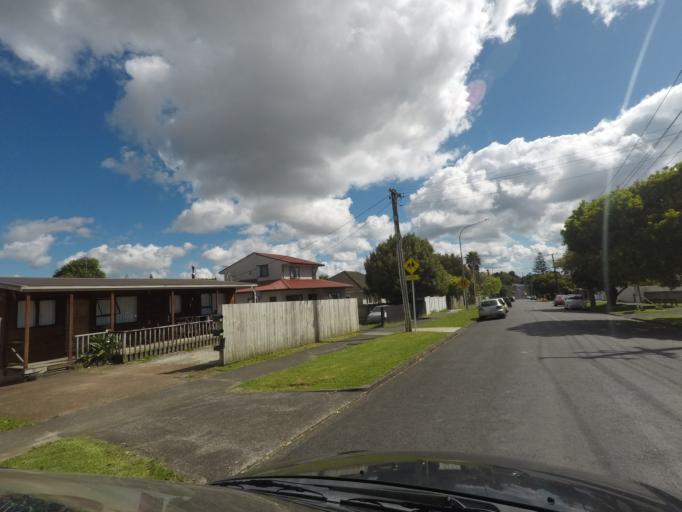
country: NZ
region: Auckland
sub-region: Auckland
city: Waitakere
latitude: -36.9143
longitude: 174.6656
